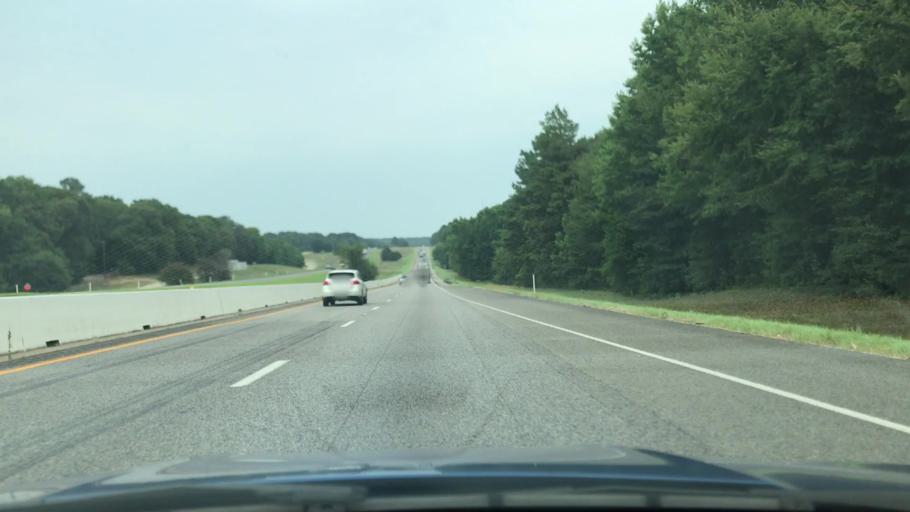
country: US
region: Texas
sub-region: Smith County
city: Lindale
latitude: 32.4682
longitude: -95.3644
